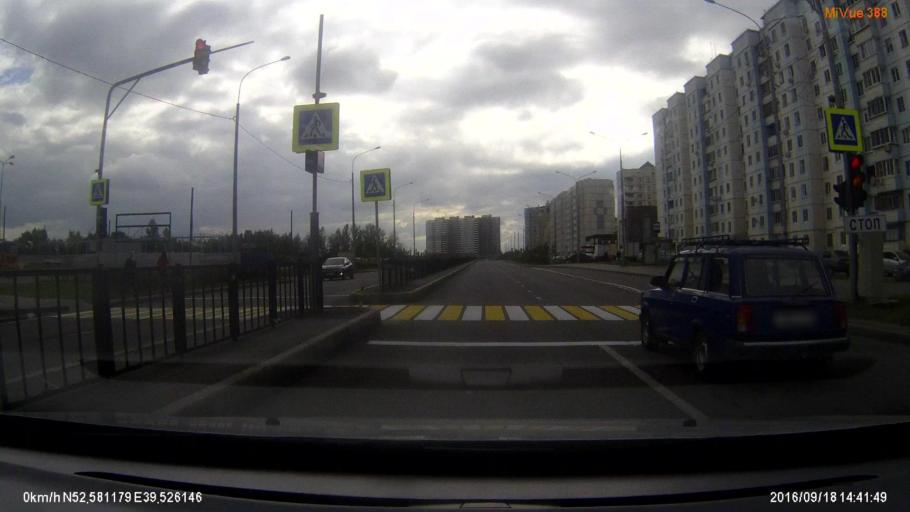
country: RU
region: Lipetsk
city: Syrskoye
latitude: 52.5812
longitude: 39.5262
